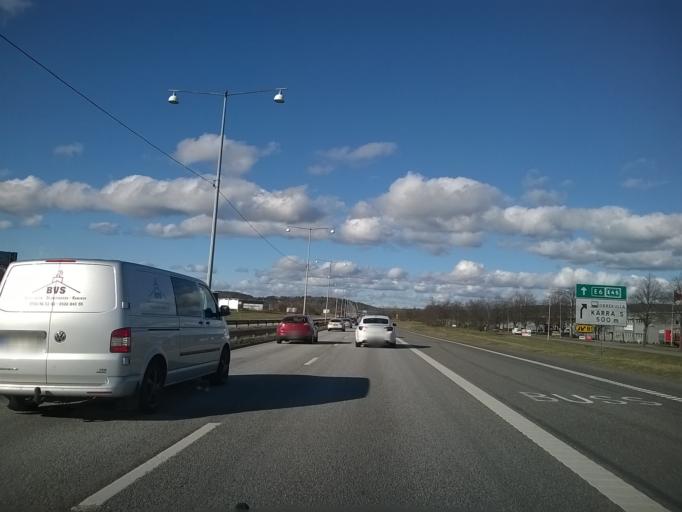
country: SE
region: Vaestra Goetaland
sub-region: Goteborg
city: Hammarkullen
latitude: 57.7780
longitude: 11.9986
